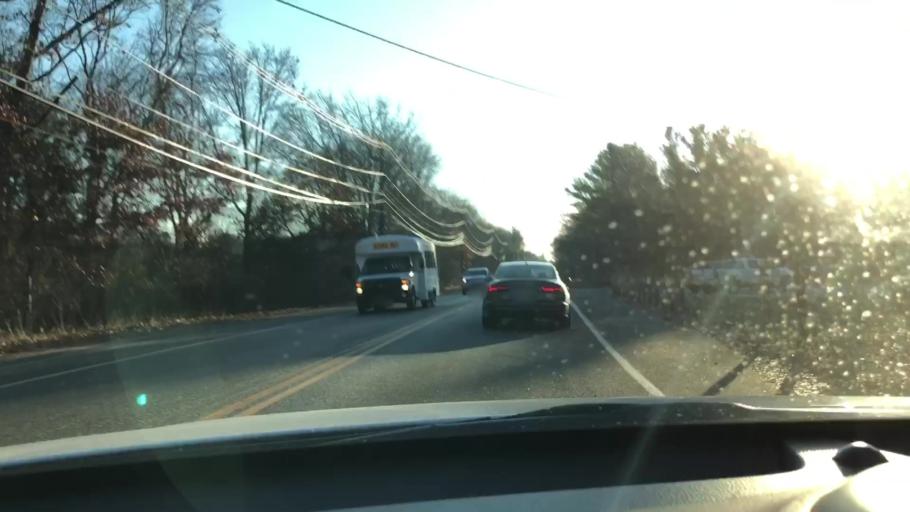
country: US
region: Massachusetts
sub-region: Plymouth County
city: Rockland
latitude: 42.1643
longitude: -70.8904
